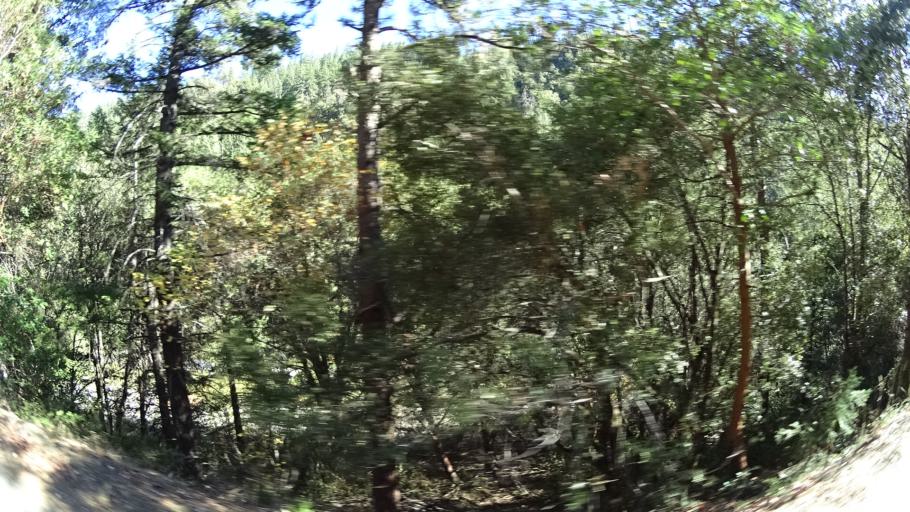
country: US
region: California
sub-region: Humboldt County
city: Willow Creek
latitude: 41.2614
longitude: -123.3184
